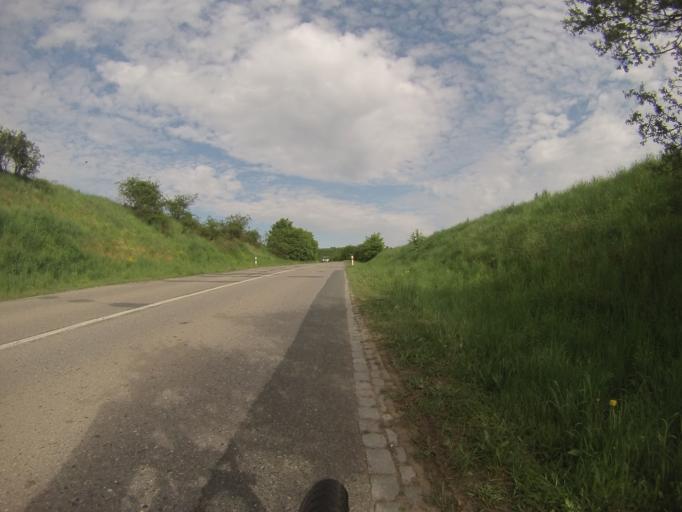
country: CZ
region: South Moravian
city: Veverska Bityska
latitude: 49.2528
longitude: 16.4525
